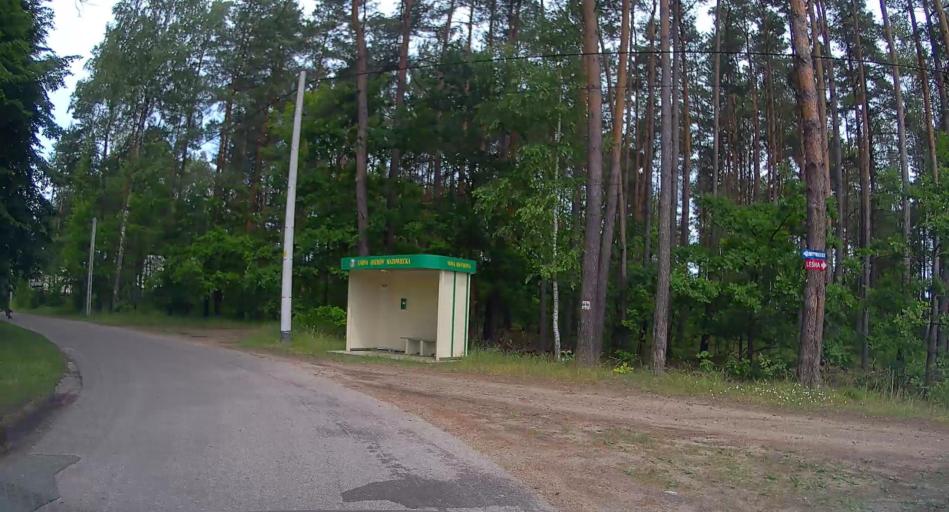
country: PL
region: Masovian Voivodeship
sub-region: Powiat ostrowski
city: Brok
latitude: 52.7421
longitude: 21.7473
